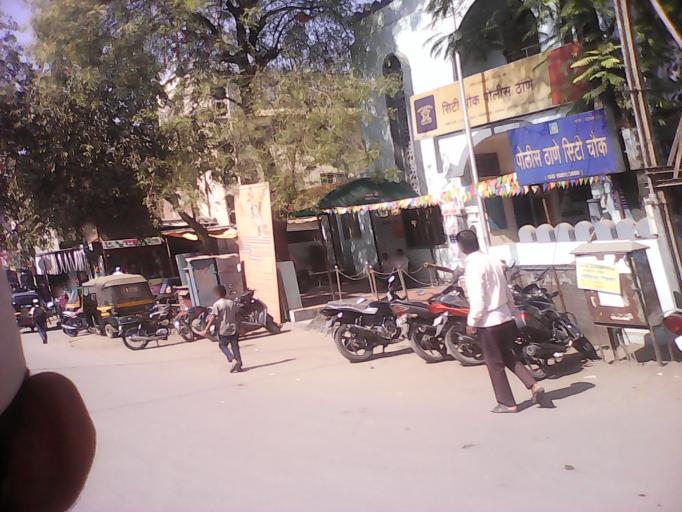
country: IN
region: Maharashtra
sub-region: Aurangabad Division
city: Aurangabad
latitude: 19.8884
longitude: 75.3315
